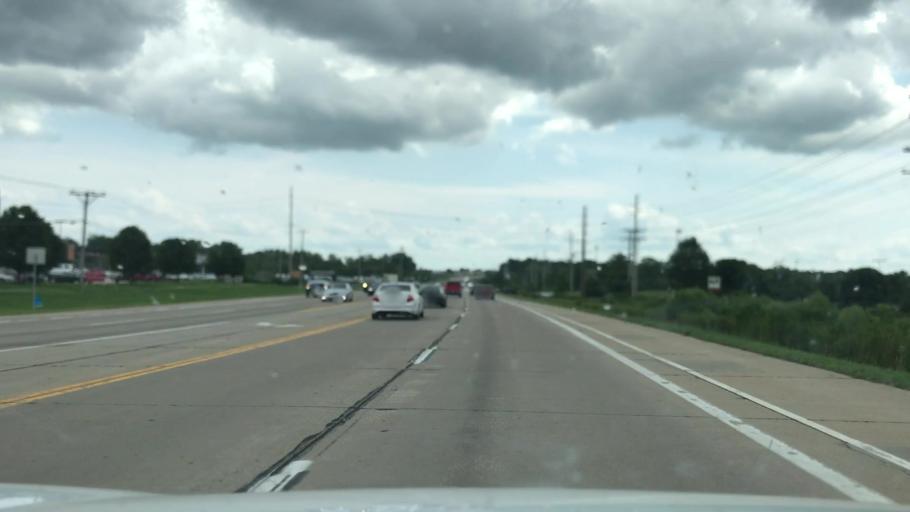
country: US
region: Missouri
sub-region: Saint Charles County
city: Weldon Spring
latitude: 38.7452
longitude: -90.6984
